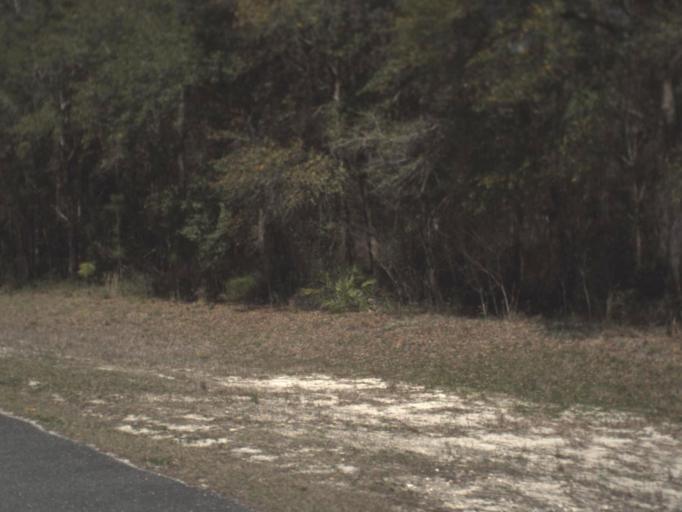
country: US
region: Florida
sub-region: Wakulla County
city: Crawfordville
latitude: 30.2874
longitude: -84.4009
